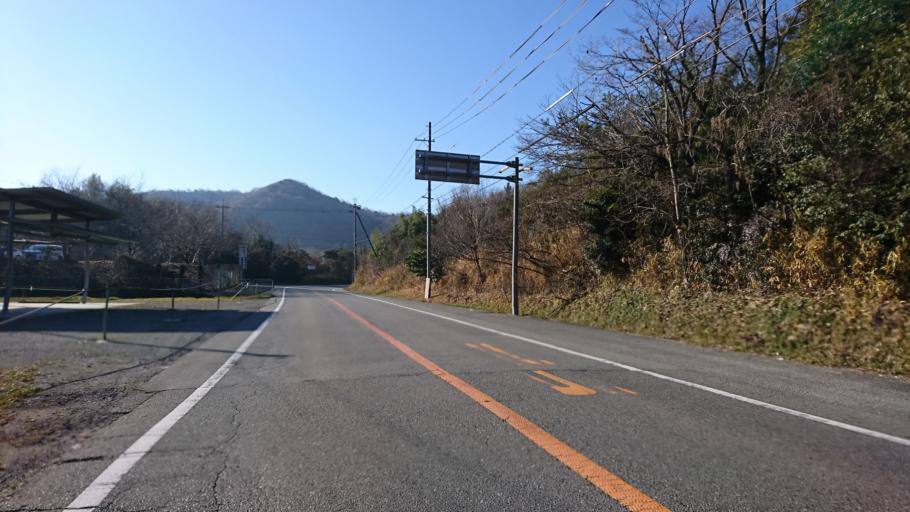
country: JP
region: Hyogo
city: Kakogawacho-honmachi
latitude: 34.8553
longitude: 134.8423
